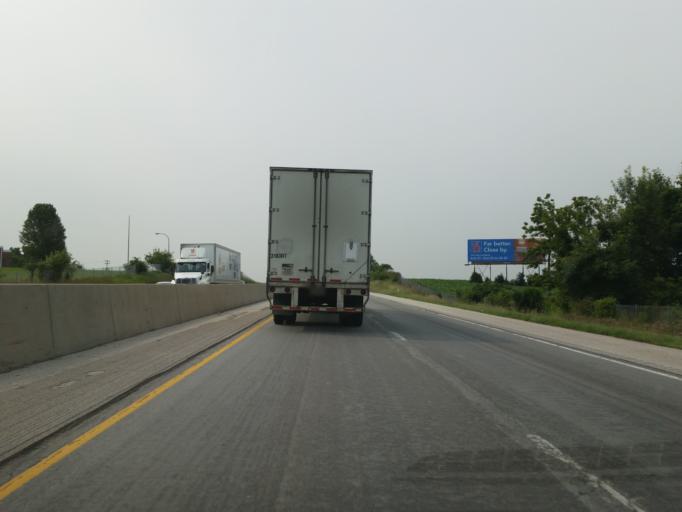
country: US
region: Pennsylvania
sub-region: York County
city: Manchester
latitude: 40.0492
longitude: -76.7506
